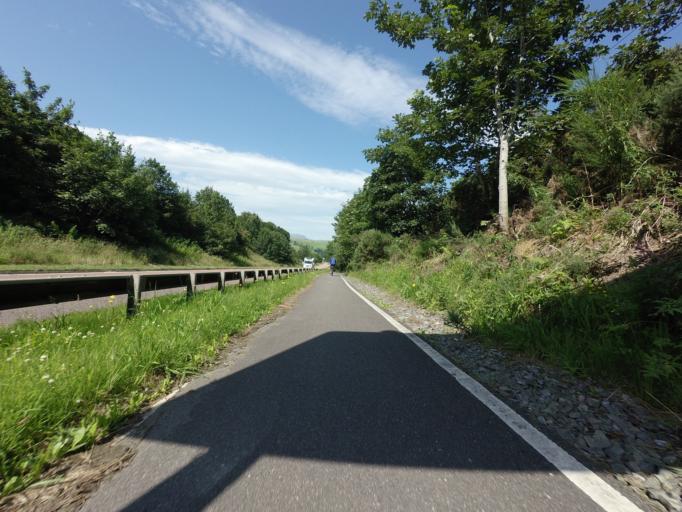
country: GB
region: Scotland
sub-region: Highland
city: Conon Bridge
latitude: 57.5691
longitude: -4.4262
